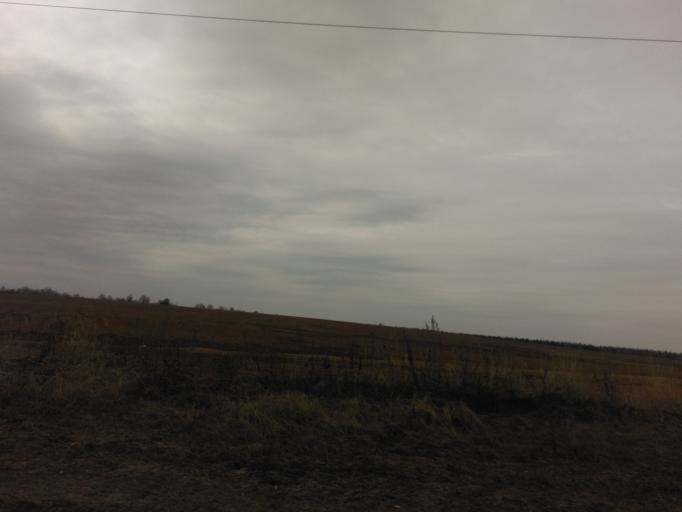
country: RU
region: Moskovskaya
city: Zvenigorod
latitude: 55.7423
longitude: 36.9329
